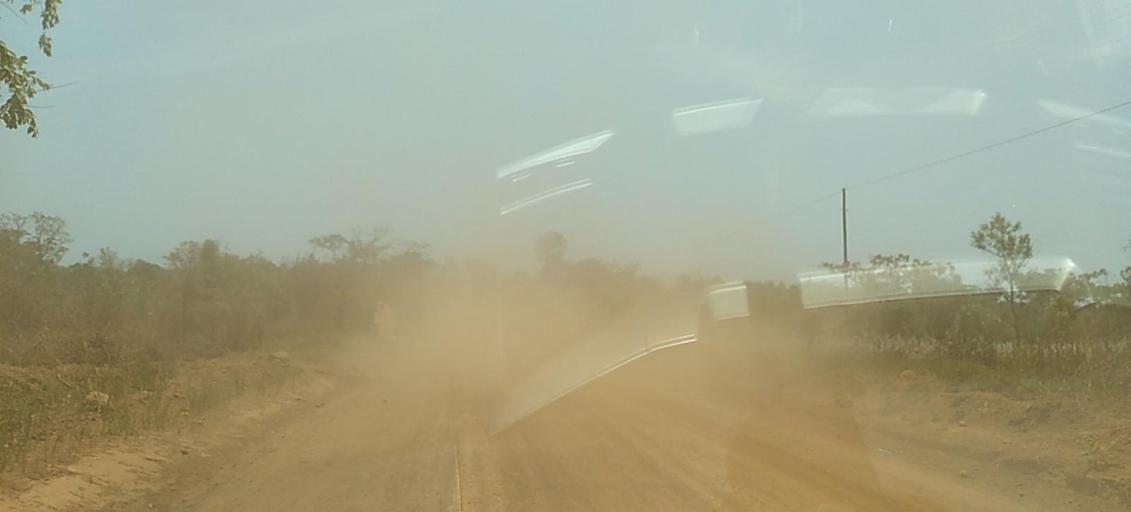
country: CD
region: Katanga
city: Kipushi
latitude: -11.8616
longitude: 27.1168
